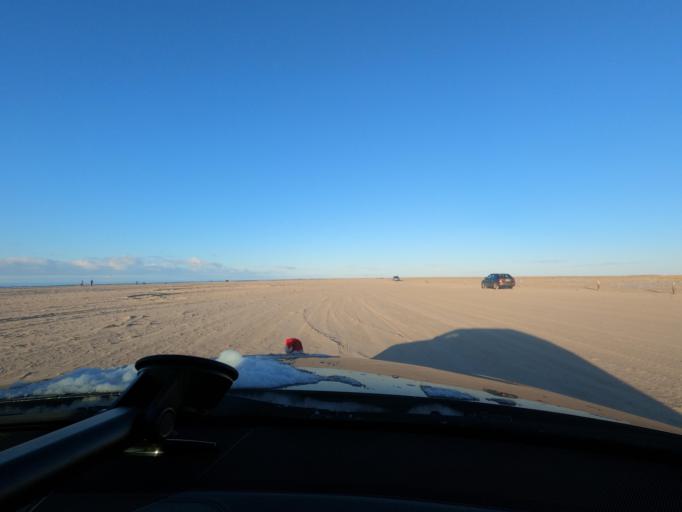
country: DE
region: Schleswig-Holstein
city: List
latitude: 55.1568
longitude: 8.4787
